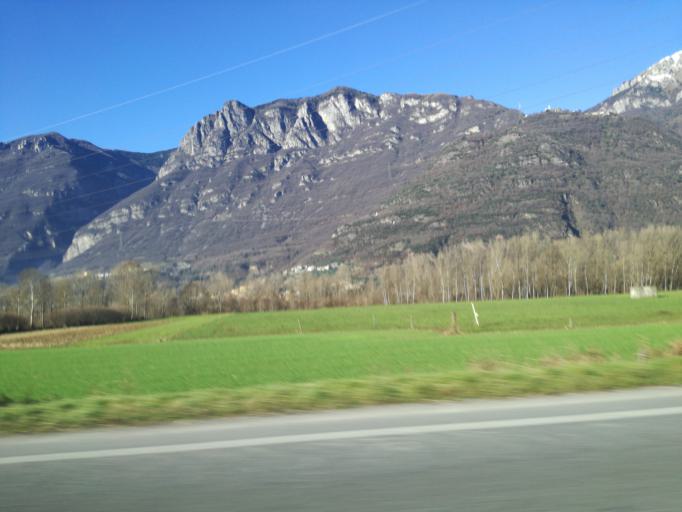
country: IT
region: Lombardy
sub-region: Provincia di Brescia
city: Pian Camuno
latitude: 45.8453
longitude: 10.1359
